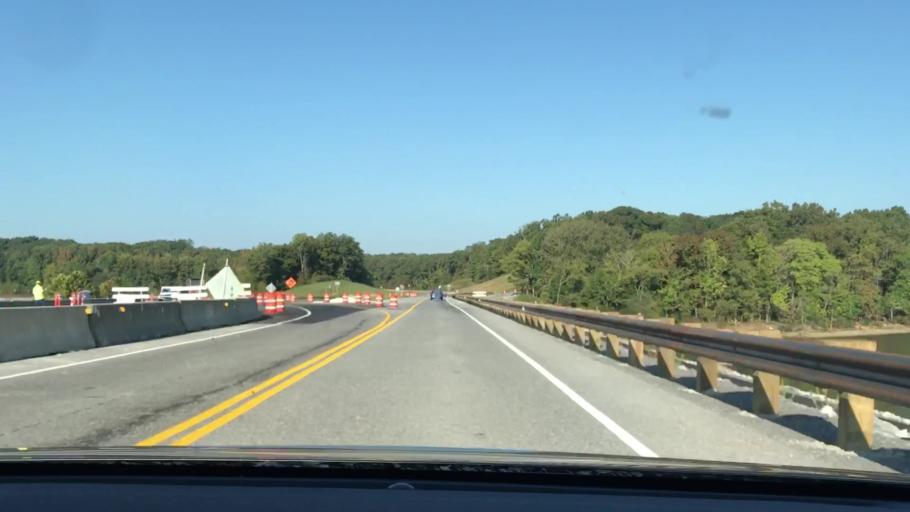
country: US
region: Kentucky
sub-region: Trigg County
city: Cadiz
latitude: 36.8019
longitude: -87.9835
